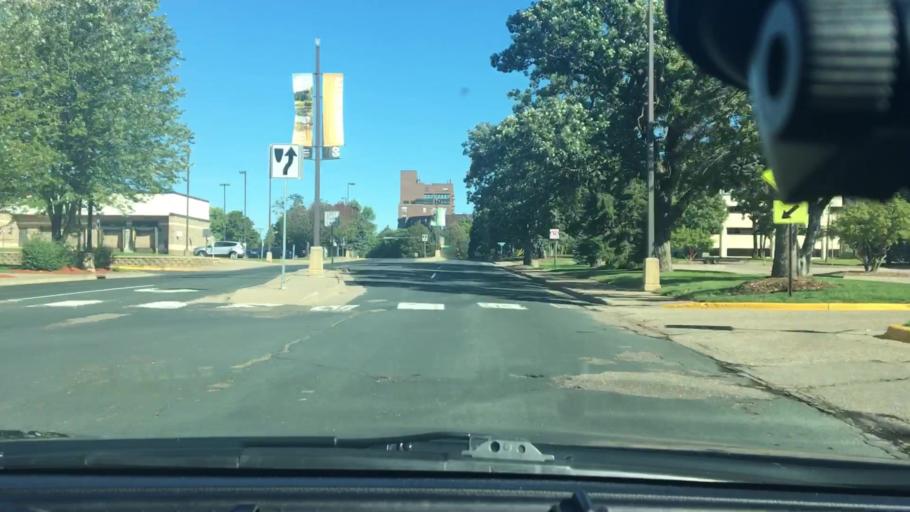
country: US
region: Minnesota
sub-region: Hennepin County
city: Golden Valley
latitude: 44.9842
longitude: -93.3772
